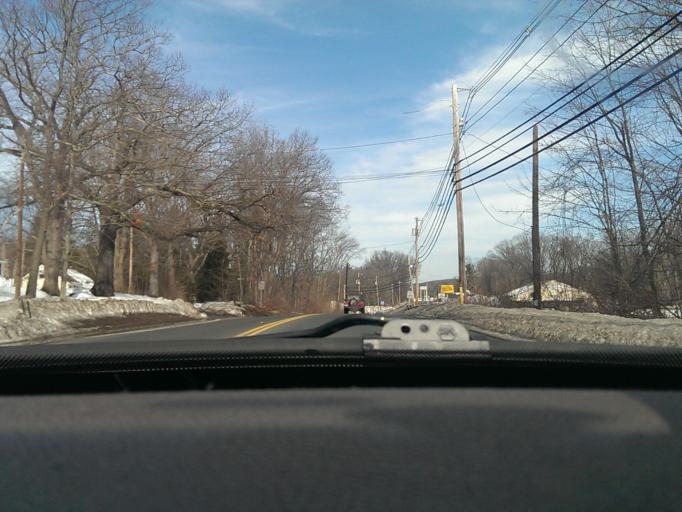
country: US
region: Massachusetts
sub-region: Hampden County
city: Three Rivers
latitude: 42.1579
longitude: -72.3618
